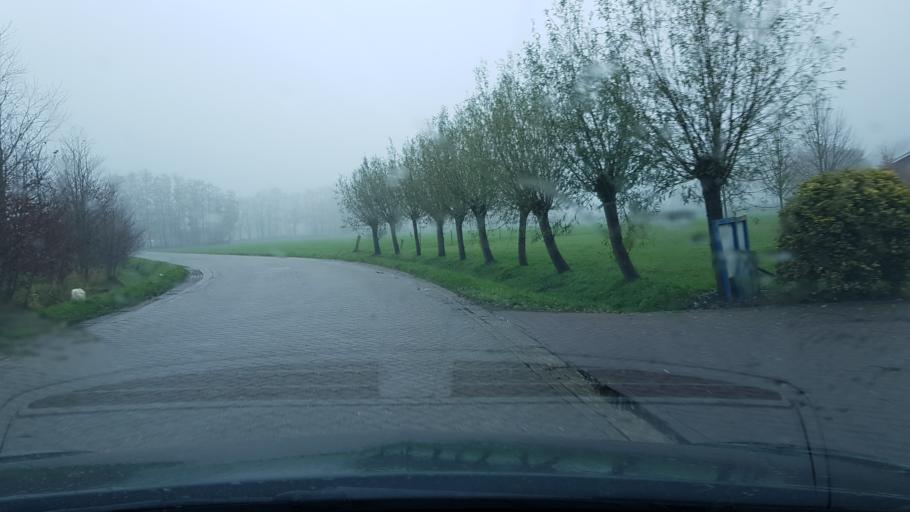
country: NL
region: Gelderland
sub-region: Gemeente Ermelo
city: Horst
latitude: 52.2674
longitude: 5.5583
